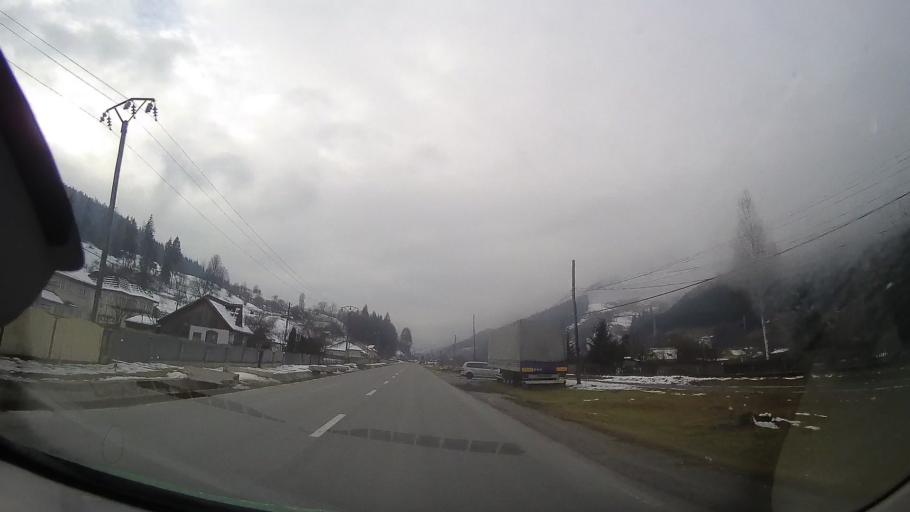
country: RO
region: Neamt
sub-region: Comuna Tasca
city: Tasca
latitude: 46.8888
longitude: 26.0127
